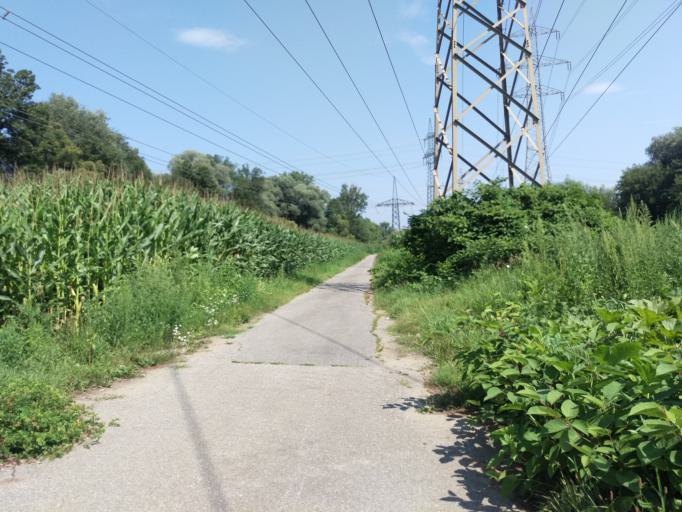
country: AT
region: Styria
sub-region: Politischer Bezirk Graz-Umgebung
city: Werndorf
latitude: 46.9113
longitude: 15.4834
